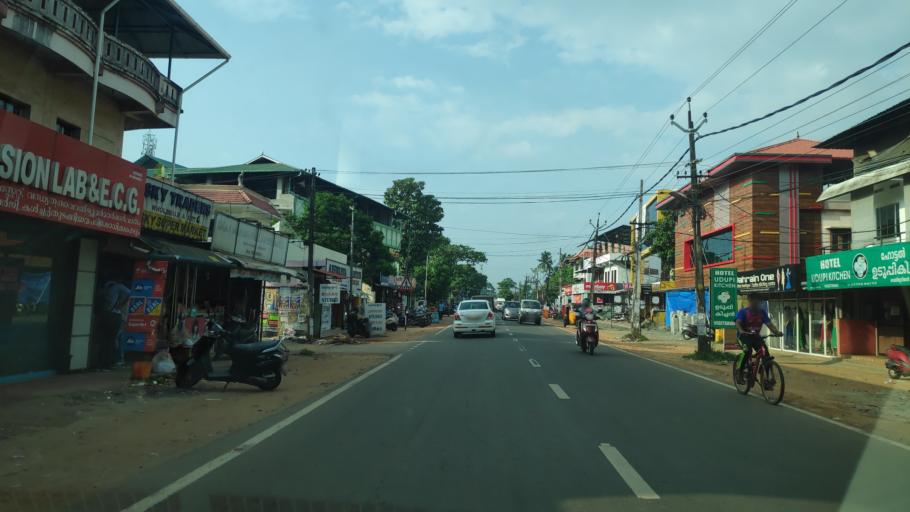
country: IN
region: Kerala
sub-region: Alappuzha
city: Alleppey
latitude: 9.5111
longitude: 76.3387
